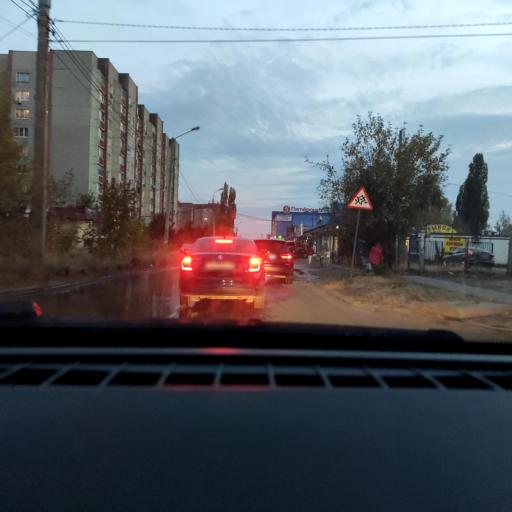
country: RU
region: Voronezj
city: Somovo
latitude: 51.7382
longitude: 39.2913
